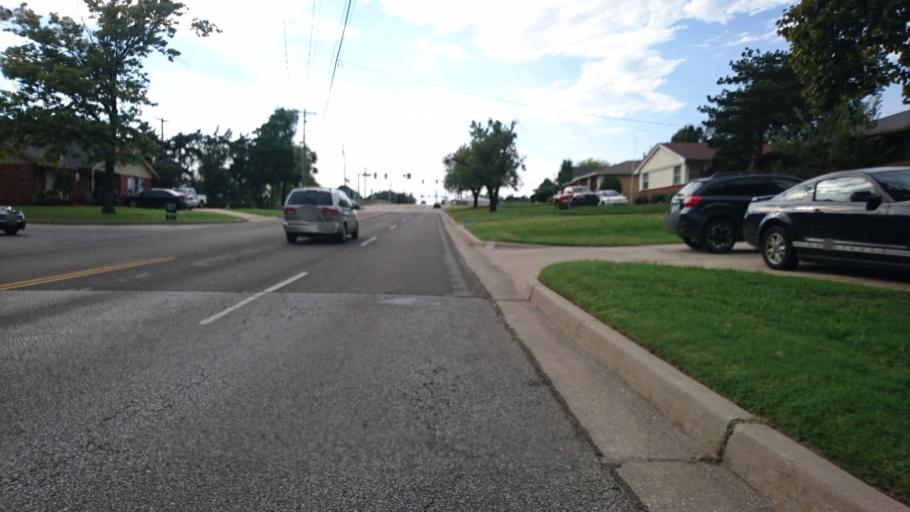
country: US
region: Oklahoma
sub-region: Oklahoma County
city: Warr Acres
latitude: 35.5078
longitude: -97.5737
